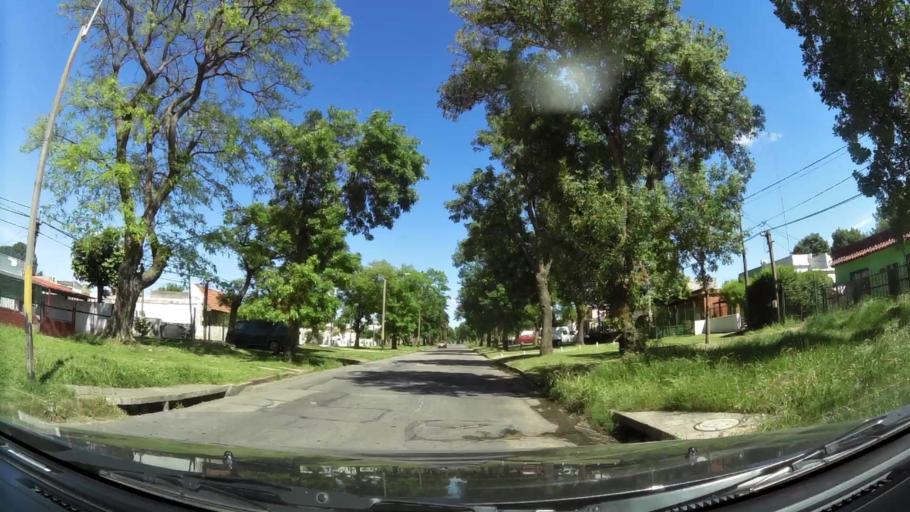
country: UY
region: Canelones
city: Paso de Carrasco
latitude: -34.8438
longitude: -56.1208
